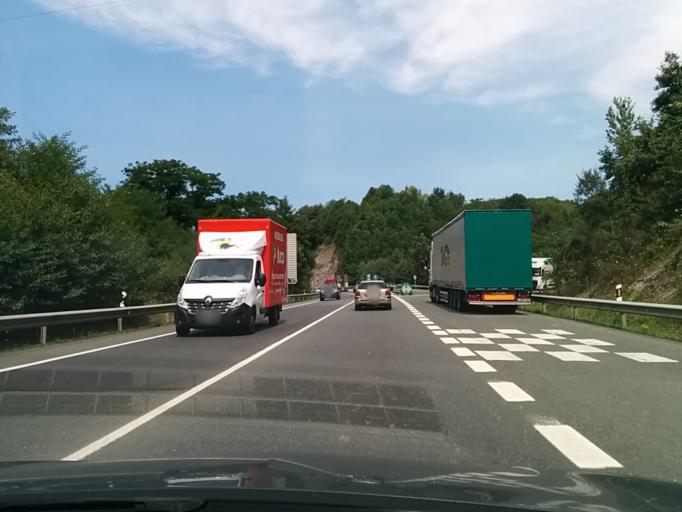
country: ES
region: Basque Country
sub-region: Provincia de Guipuzcoa
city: Lezo
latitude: 43.3127
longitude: -1.8920
